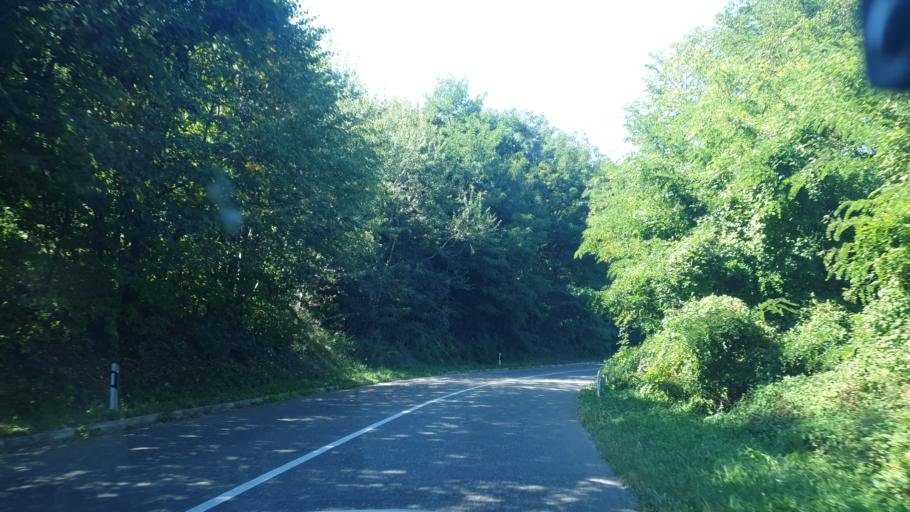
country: RS
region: Central Serbia
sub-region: Kolubarski Okrug
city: Mionica
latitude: 44.1751
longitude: 20.0146
